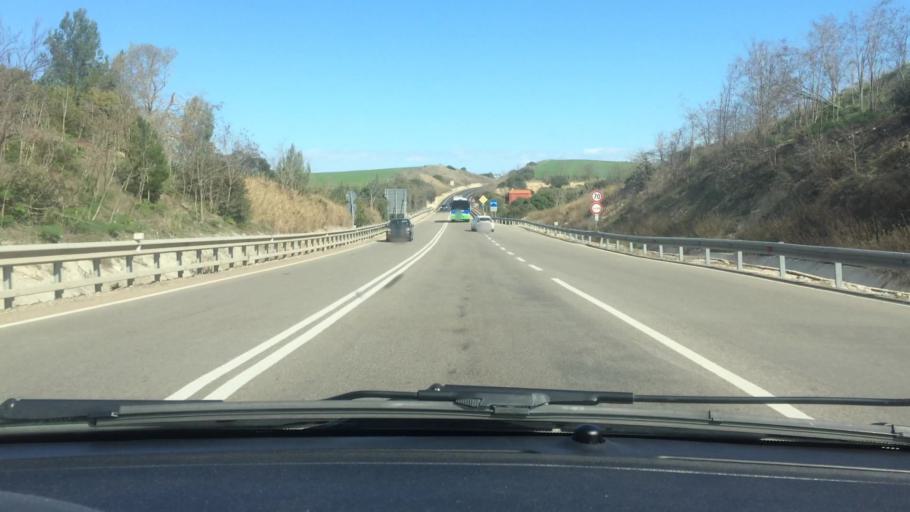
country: IT
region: Basilicate
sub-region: Provincia di Matera
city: La Martella
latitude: 40.5973
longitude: 16.5658
